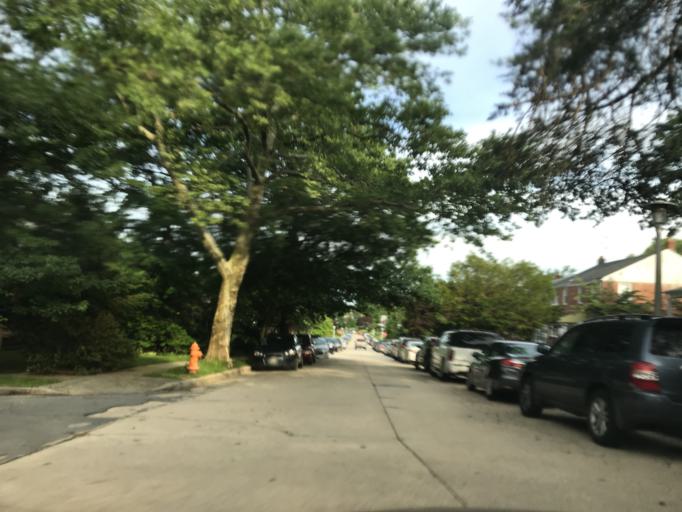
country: US
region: Maryland
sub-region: Baltimore County
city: Towson
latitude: 39.3628
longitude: -76.6032
